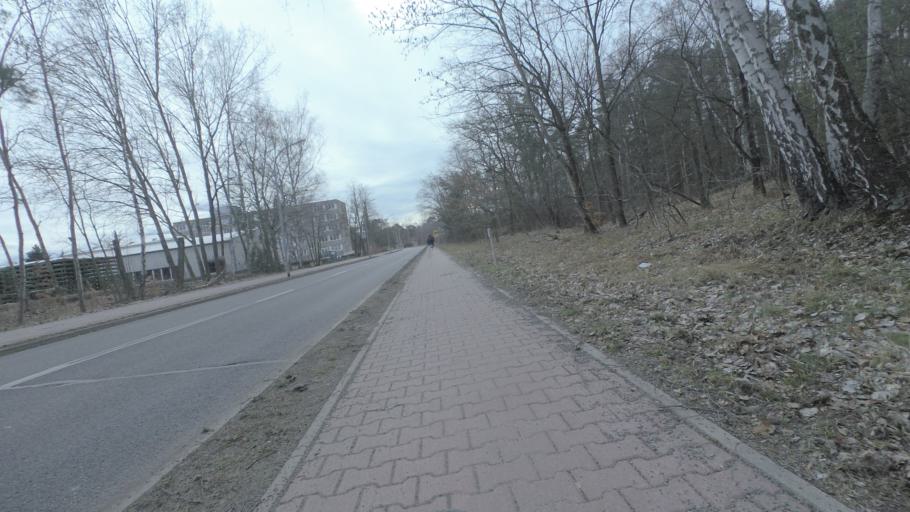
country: DE
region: Brandenburg
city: Ludwigsfelde
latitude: 52.3179
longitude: 13.2656
